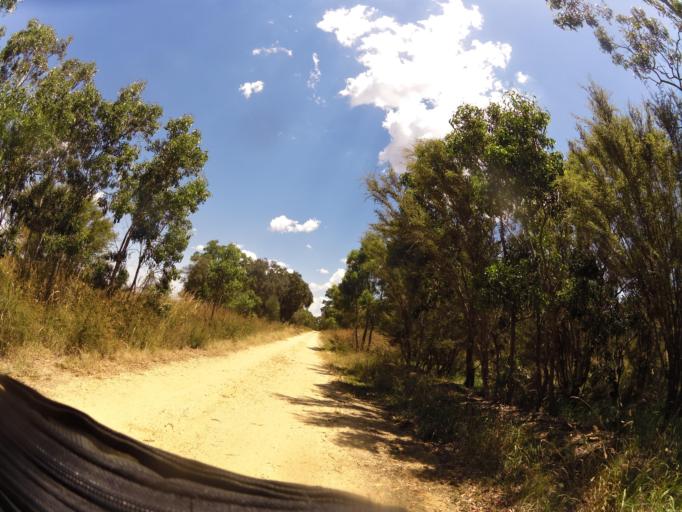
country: AU
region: Victoria
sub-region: Wellington
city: Heyfield
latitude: -37.9788
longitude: 146.8503
